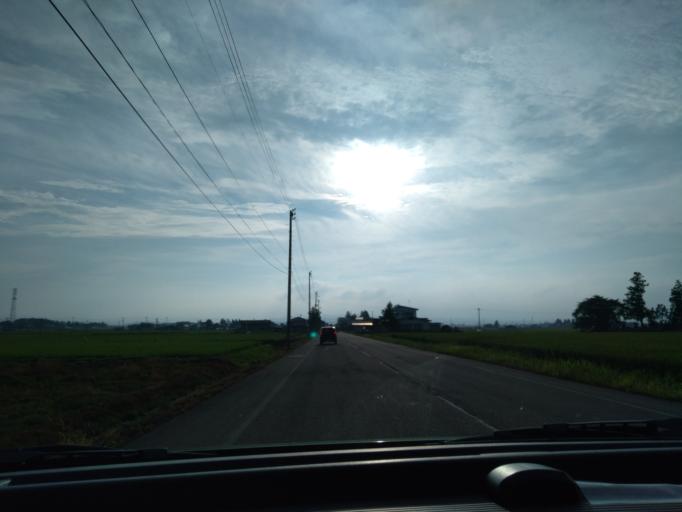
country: JP
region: Akita
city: Yokotemachi
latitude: 39.3745
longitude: 140.5405
